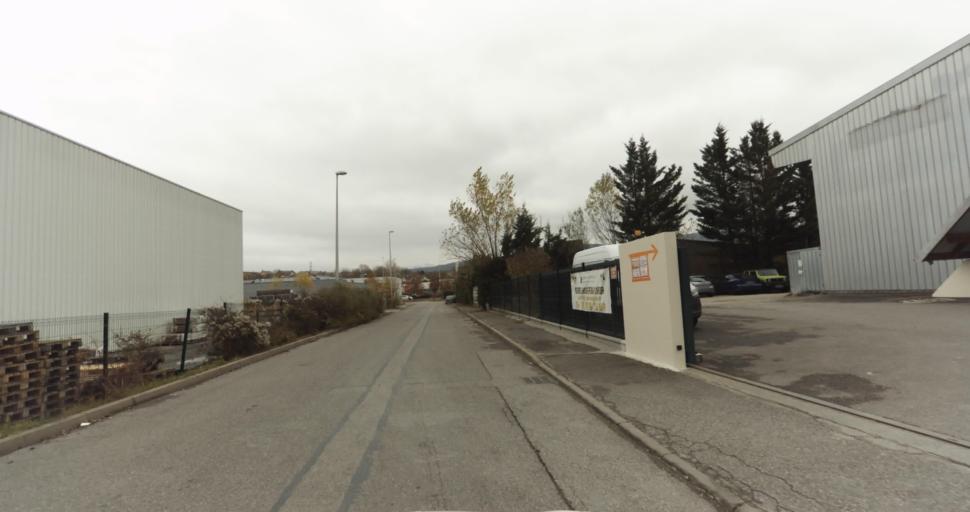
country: FR
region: Rhone-Alpes
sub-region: Departement de la Haute-Savoie
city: Seynod
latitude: 45.8856
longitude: 6.0719
